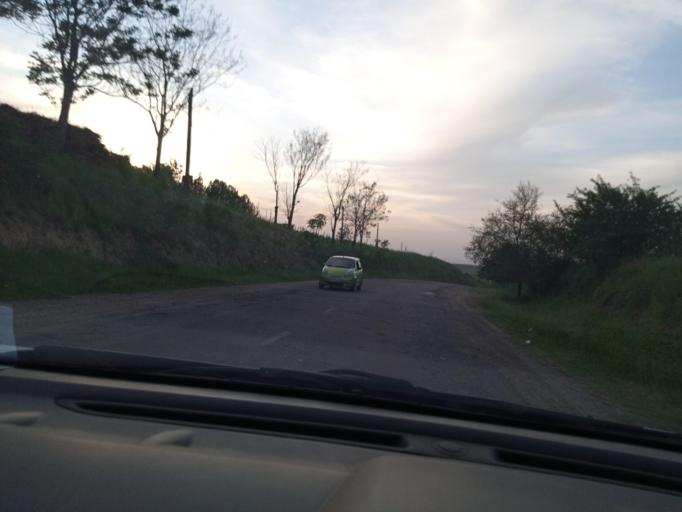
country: UZ
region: Toshkent
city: Parkent
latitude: 41.2376
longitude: 69.7347
